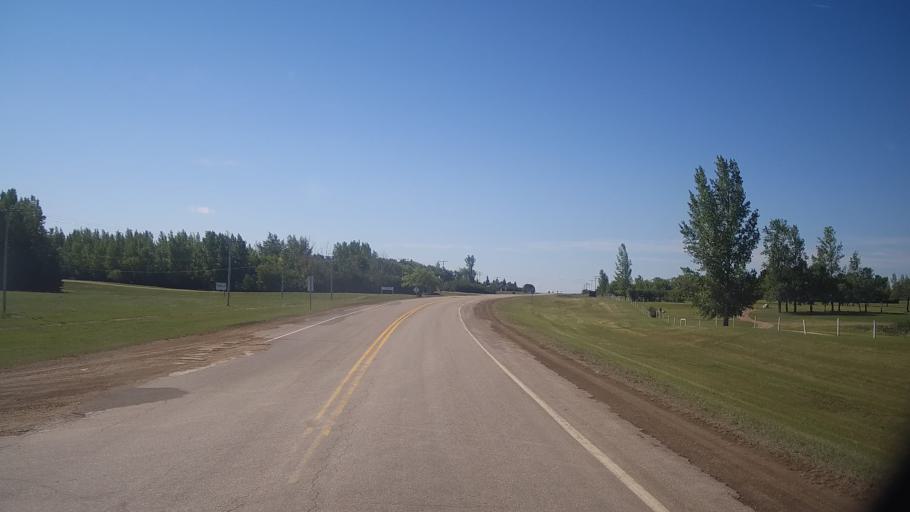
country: CA
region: Saskatchewan
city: Watrous
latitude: 51.7175
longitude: -105.4515
